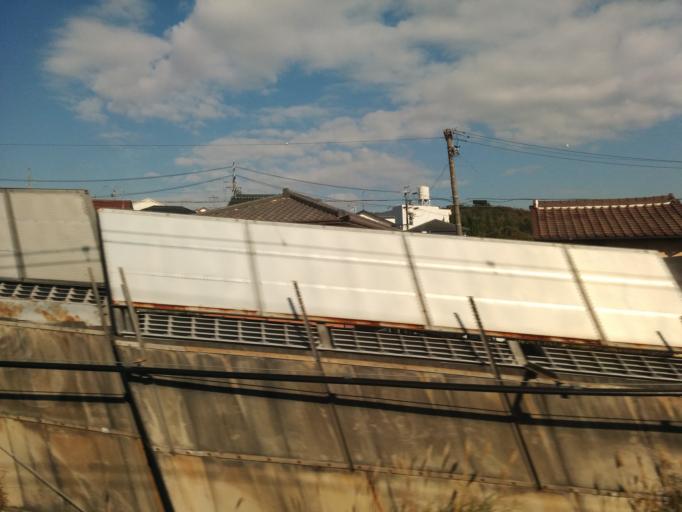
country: JP
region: Aichi
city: Obu
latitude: 35.0590
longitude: 136.9468
